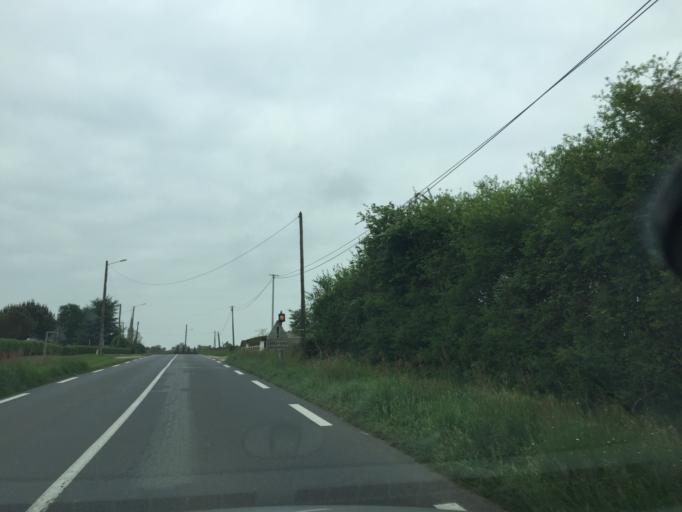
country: FR
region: Brittany
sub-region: Departement des Cotes-d'Armor
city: Henanbihen
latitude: 48.5649
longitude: -2.3708
